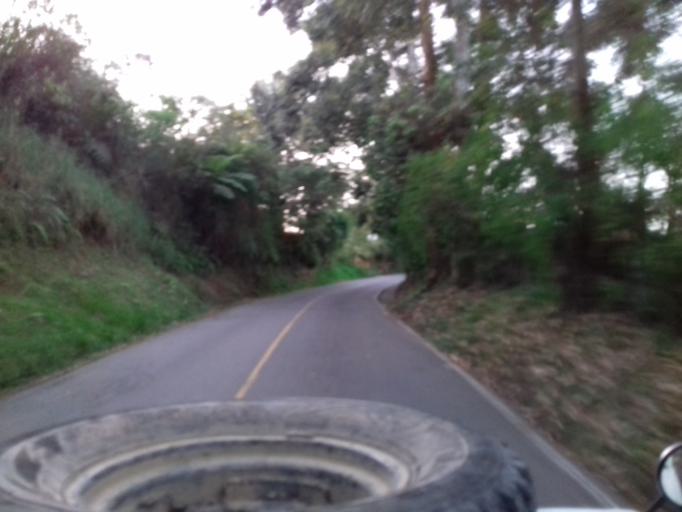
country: CO
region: Quindio
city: Salento
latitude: 4.6425
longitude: -75.5719
